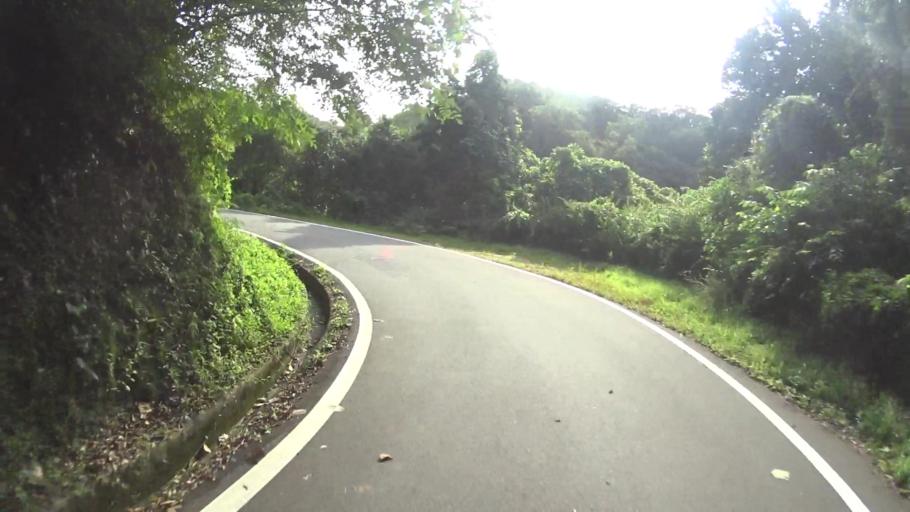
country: JP
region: Kyoto
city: Miyazu
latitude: 35.5659
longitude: 135.1238
